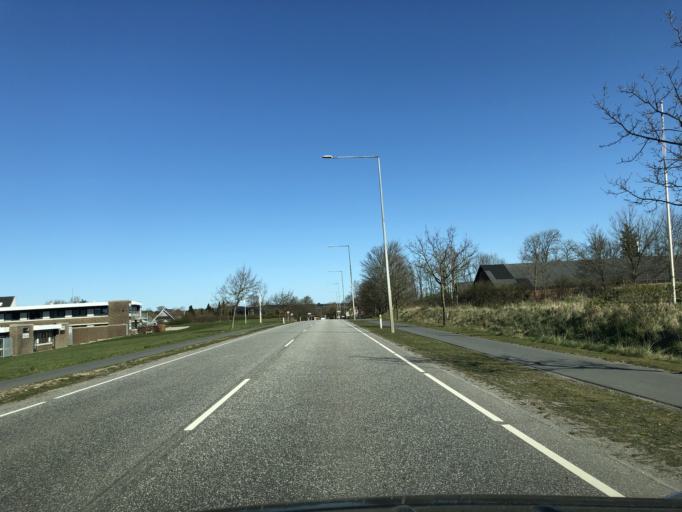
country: DK
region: North Denmark
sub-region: Rebild Kommune
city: Stovring
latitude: 56.8799
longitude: 9.8396
